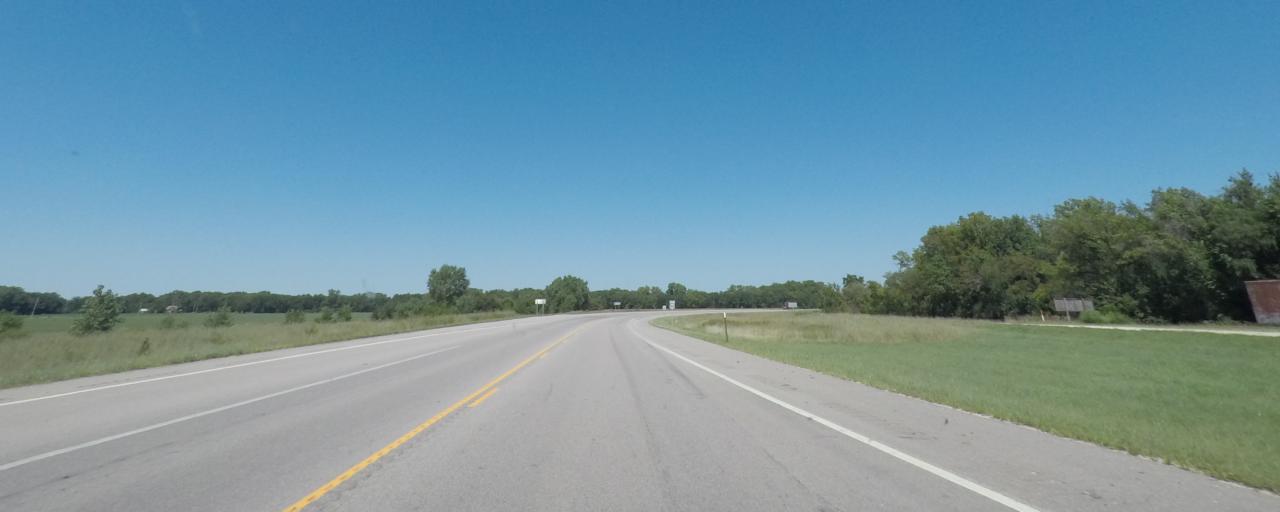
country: US
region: Kansas
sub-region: Chase County
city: Cottonwood Falls
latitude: 38.3740
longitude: -96.6499
